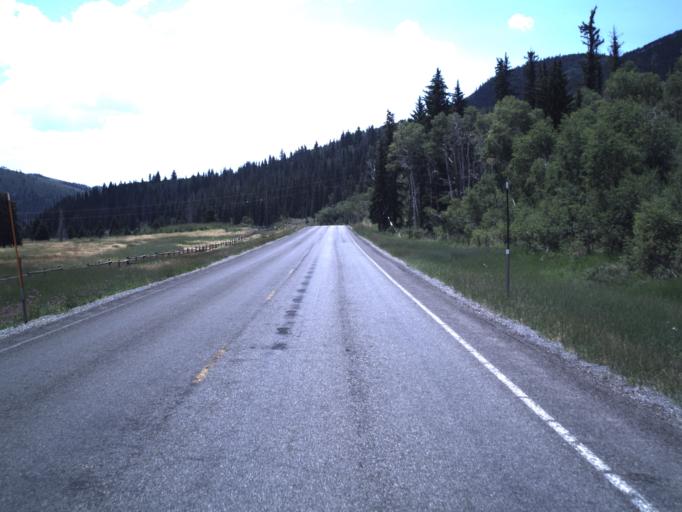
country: US
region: Utah
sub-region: Sanpete County
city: Fairview
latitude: 39.7107
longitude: -111.1633
